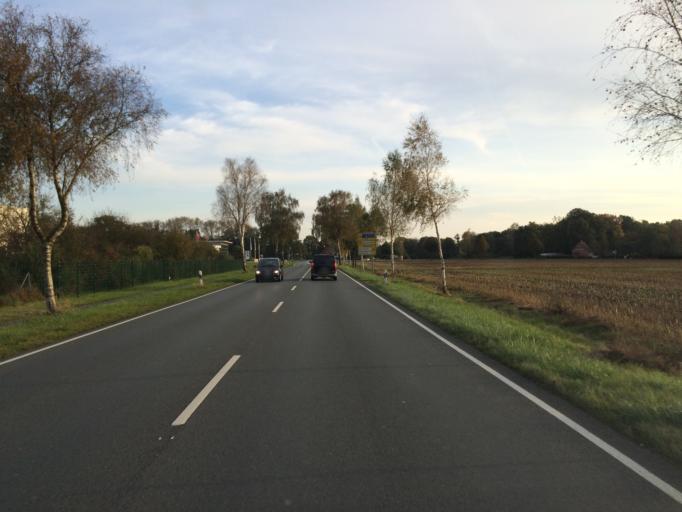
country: DE
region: Lower Saxony
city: Soltau
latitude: 52.9720
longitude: 9.8512
